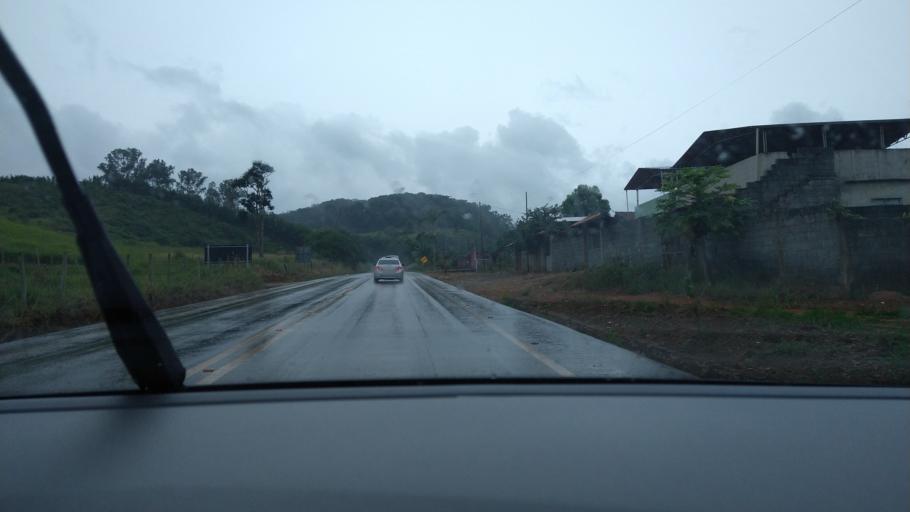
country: BR
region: Minas Gerais
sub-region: Vicosa
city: Vicosa
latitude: -20.6292
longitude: -42.8698
